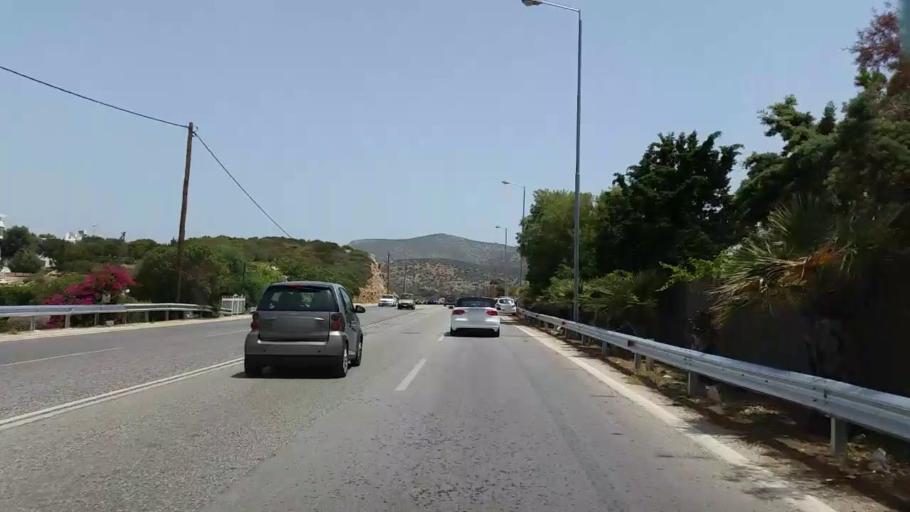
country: GR
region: Attica
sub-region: Nomarchia Anatolikis Attikis
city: Saronida
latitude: 37.7797
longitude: 23.8923
